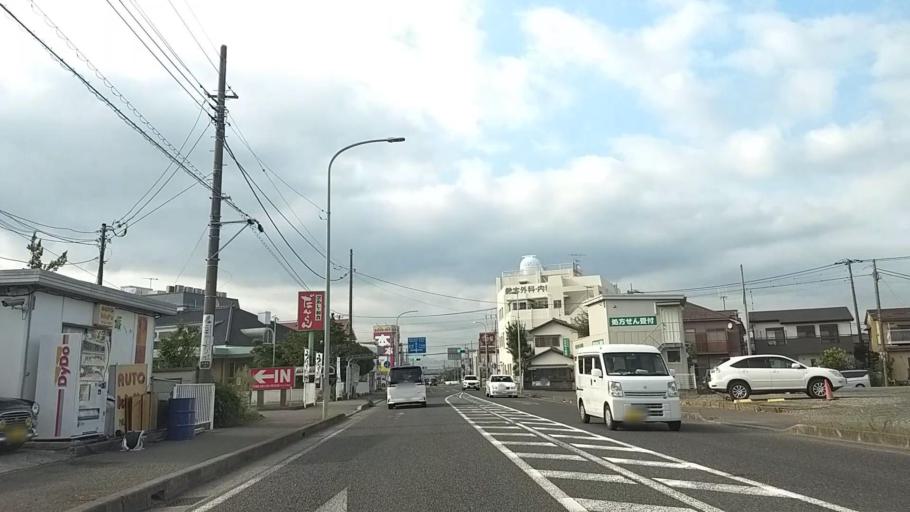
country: JP
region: Kanagawa
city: Hiratsuka
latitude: 35.3562
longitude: 139.3271
